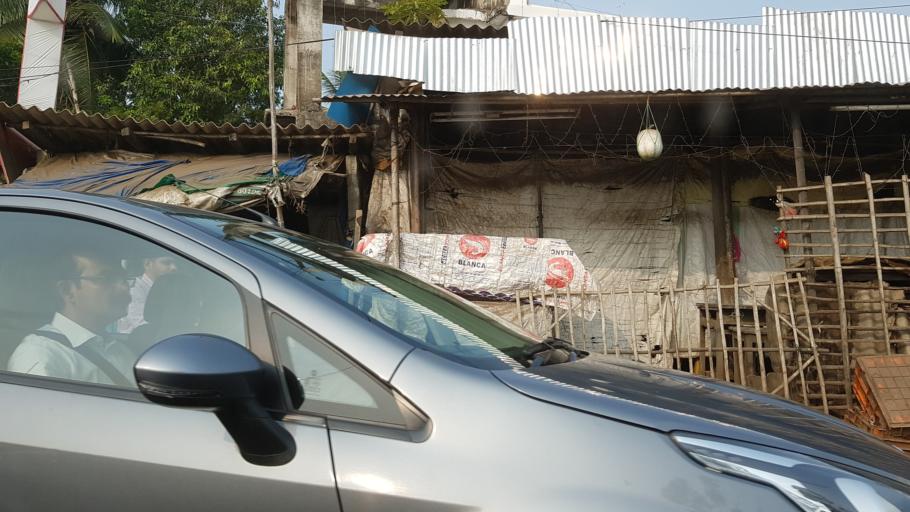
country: IN
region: Andhra Pradesh
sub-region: West Godavari
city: Akividu
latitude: 16.5372
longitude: 81.4128
